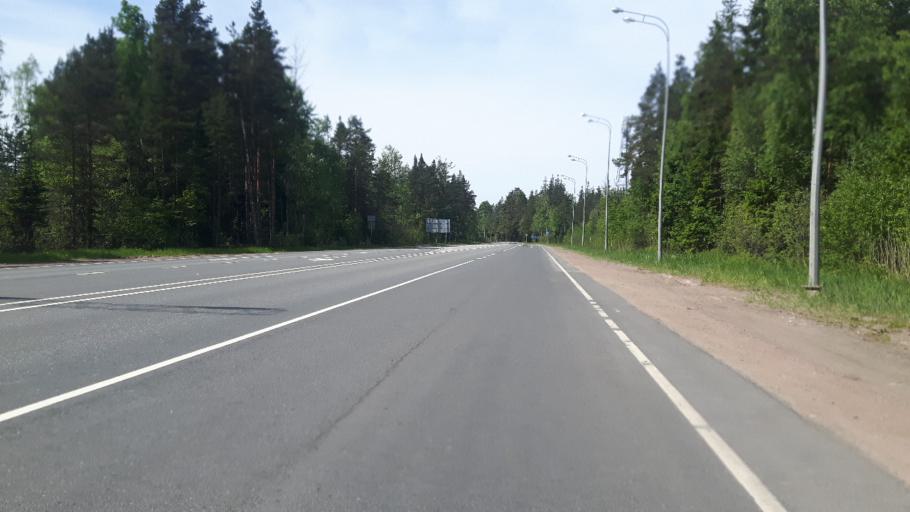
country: RU
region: Leningrad
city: Vistino
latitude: 59.6610
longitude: 28.4194
